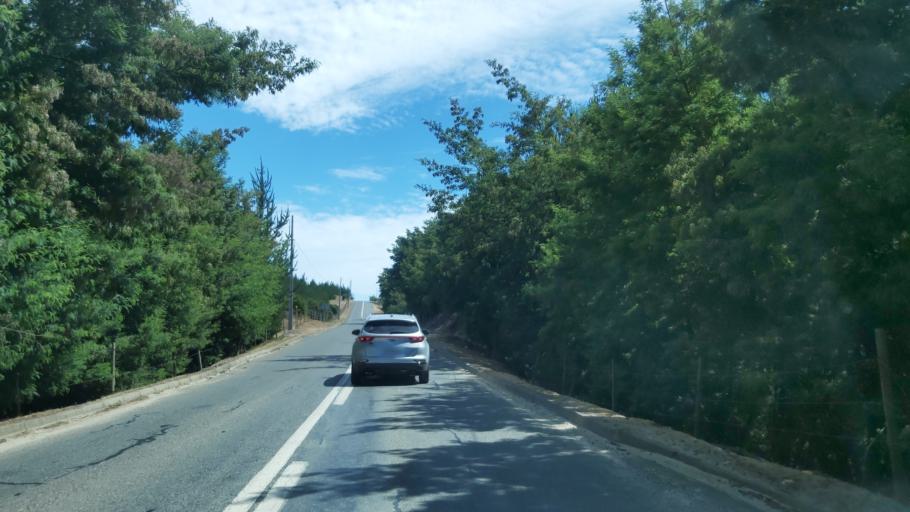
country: CL
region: Maule
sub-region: Provincia de Talca
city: Constitucion
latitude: -35.5213
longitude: -72.5351
